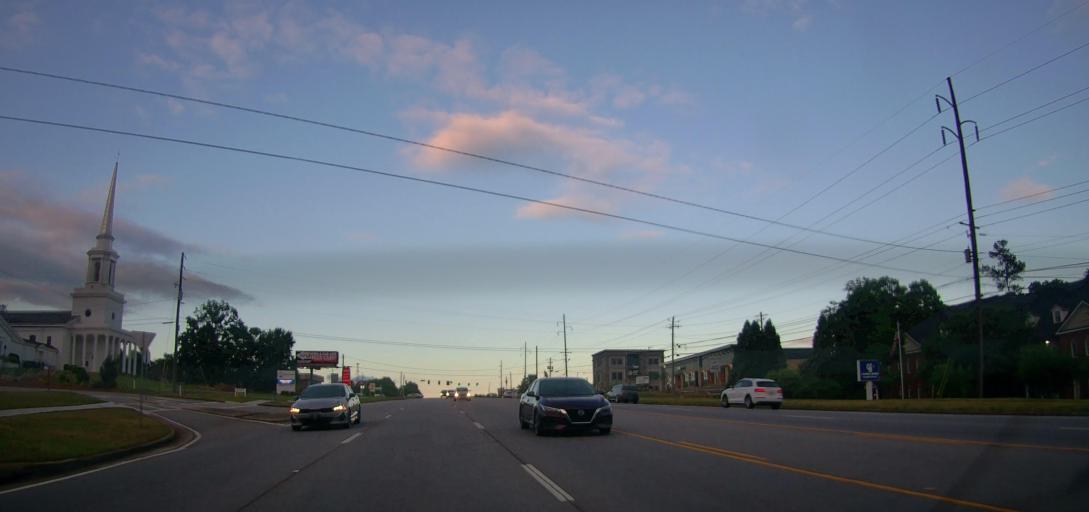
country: US
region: Georgia
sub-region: Clarke County
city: Athens
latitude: 33.9481
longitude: -83.4172
